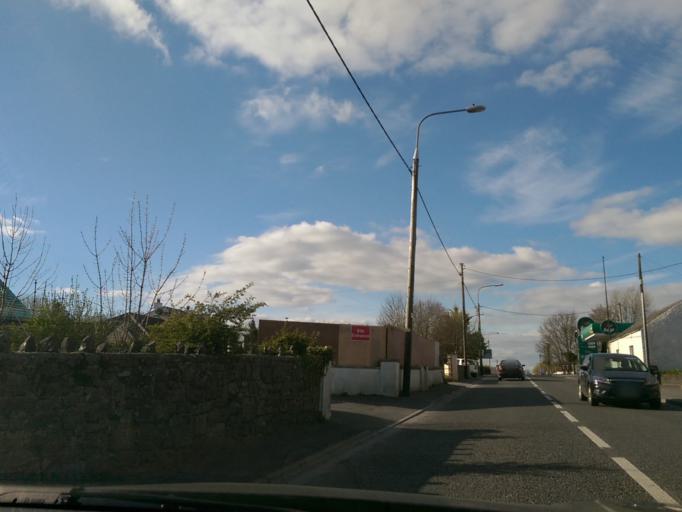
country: IE
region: Connaught
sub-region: County Galway
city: Portumna
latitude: 53.0948
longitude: -8.2245
